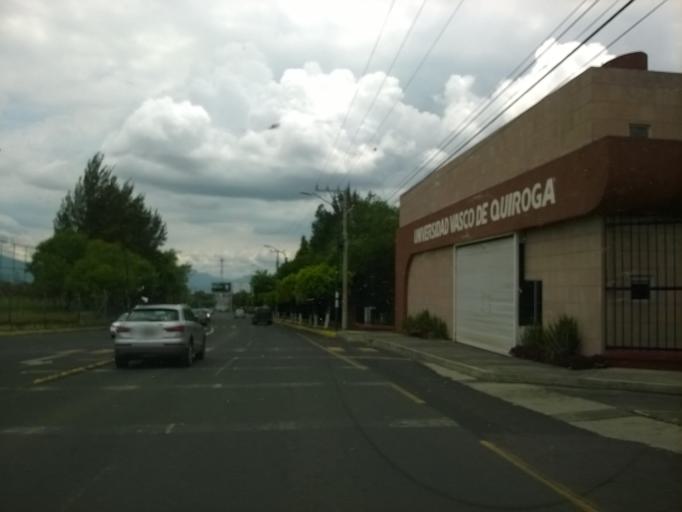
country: MX
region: Michoacan
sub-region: Morelia
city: Montana Monarca (Punta Altozano)
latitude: 19.6753
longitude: -101.1810
